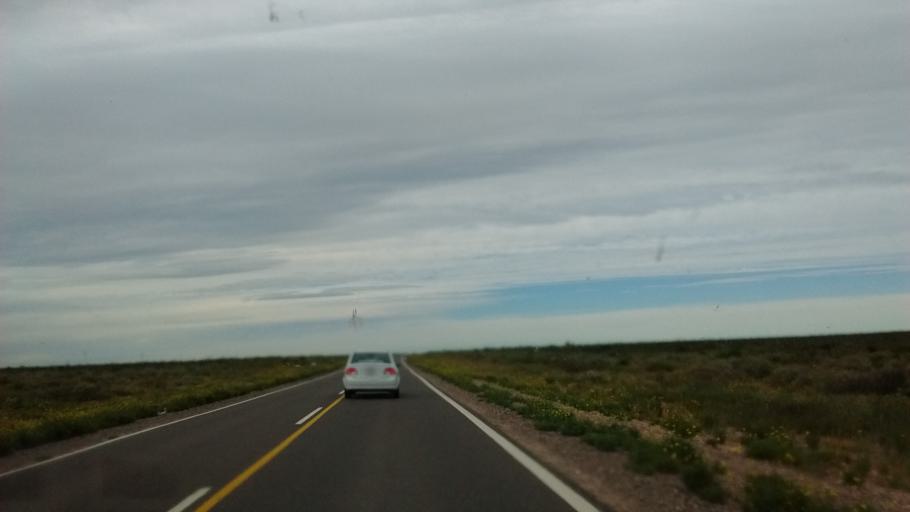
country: AR
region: Rio Negro
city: Contraalmirante Cordero
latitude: -38.3367
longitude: -68.0102
